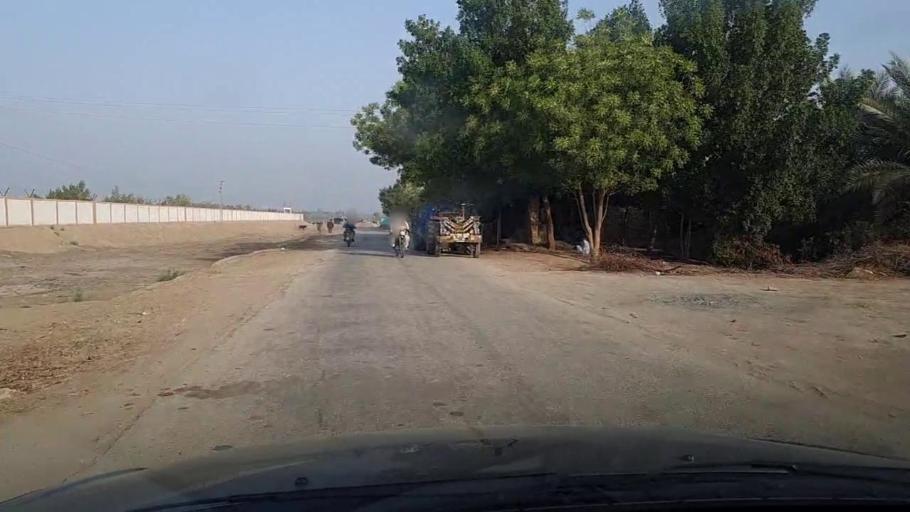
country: PK
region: Sindh
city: Khairpur
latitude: 27.5486
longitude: 68.6952
